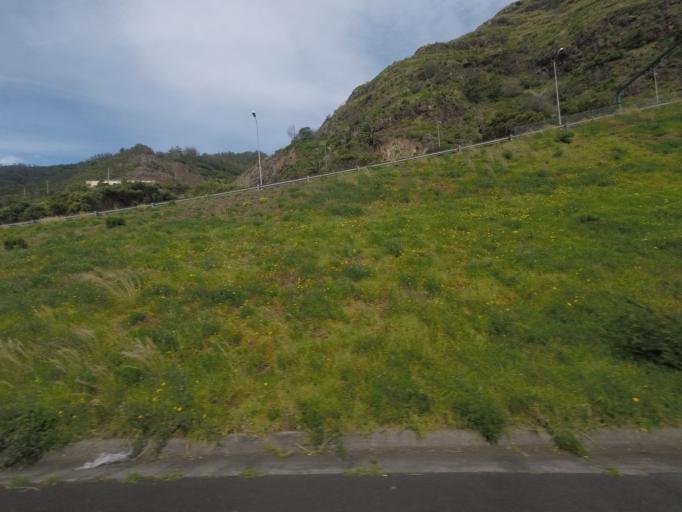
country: PT
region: Madeira
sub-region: Machico
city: Canical
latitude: 32.7381
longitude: -16.7519
